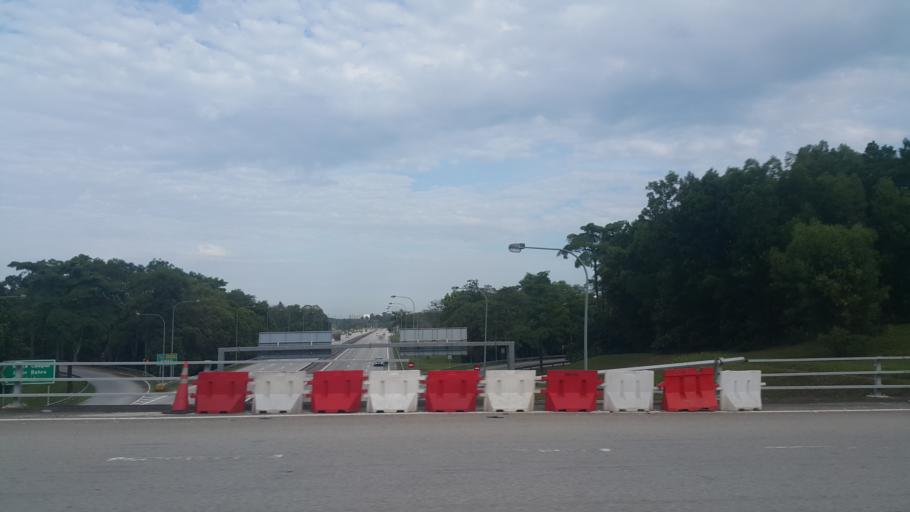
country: MY
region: Johor
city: Skudai
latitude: 1.4330
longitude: 103.6057
